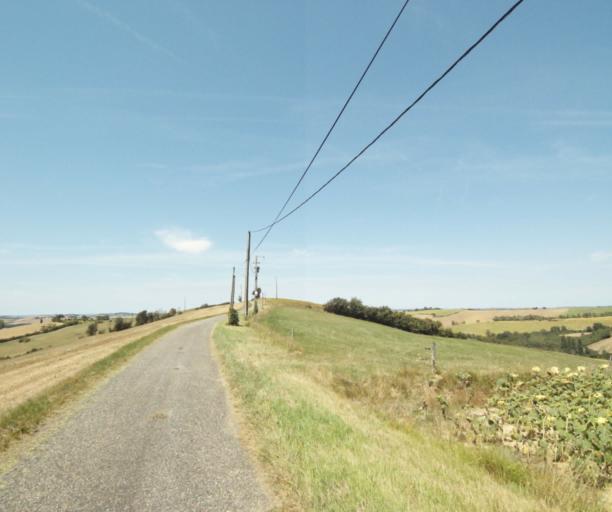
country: FR
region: Midi-Pyrenees
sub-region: Departement de l'Ariege
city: Lezat-sur-Leze
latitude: 43.3074
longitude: 1.3593
